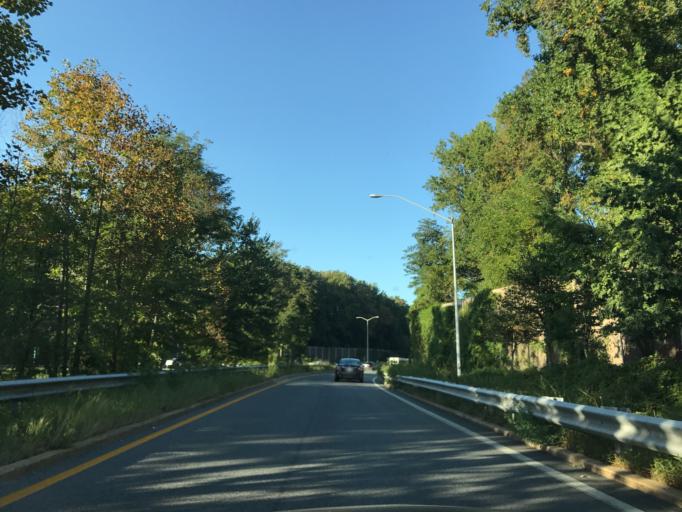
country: US
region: Maryland
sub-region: Baltimore County
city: Pikesville
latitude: 39.3959
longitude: -76.6856
